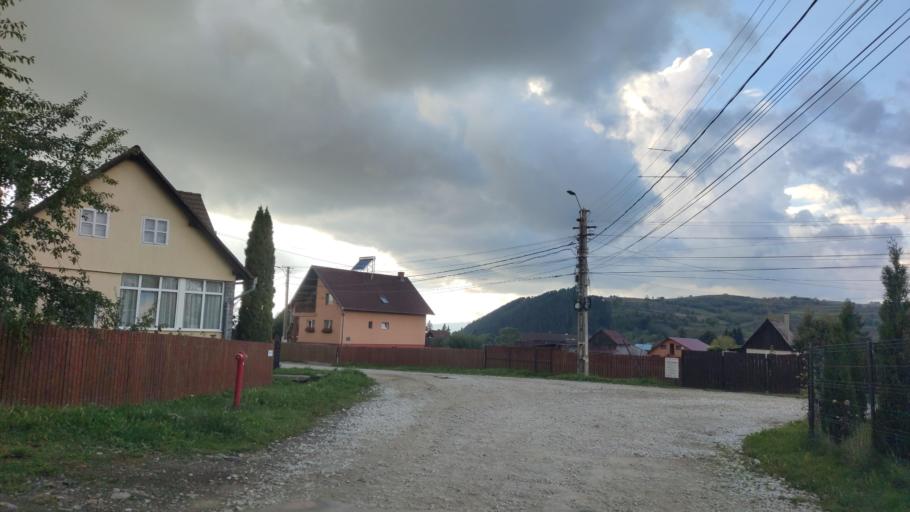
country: RO
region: Harghita
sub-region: Municipiul Gheorgheni
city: Gheorgheni
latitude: 46.7236
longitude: 25.6347
